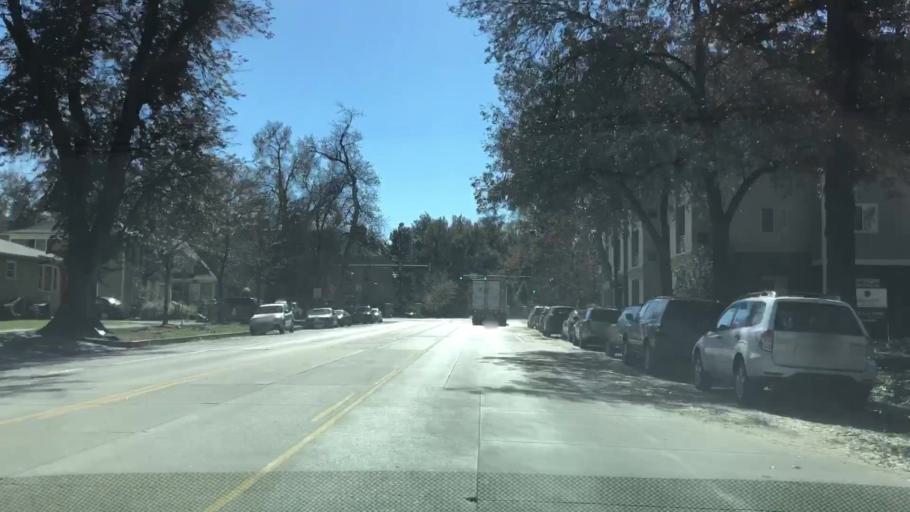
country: US
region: Colorado
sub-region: Larimer County
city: Fort Collins
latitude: 40.5791
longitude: -105.0807
